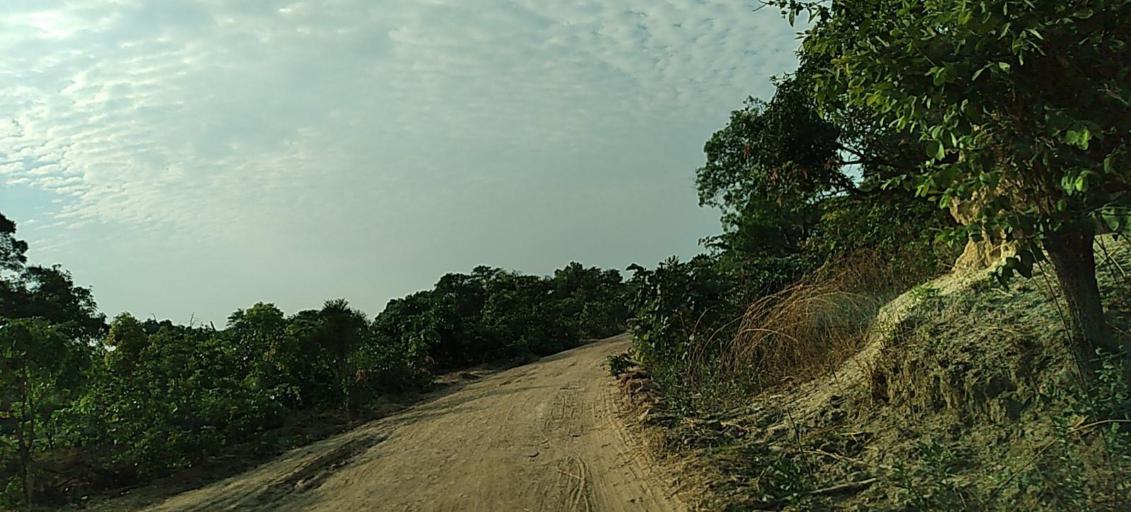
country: ZM
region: Copperbelt
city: Chingola
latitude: -12.8693
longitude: 27.6876
